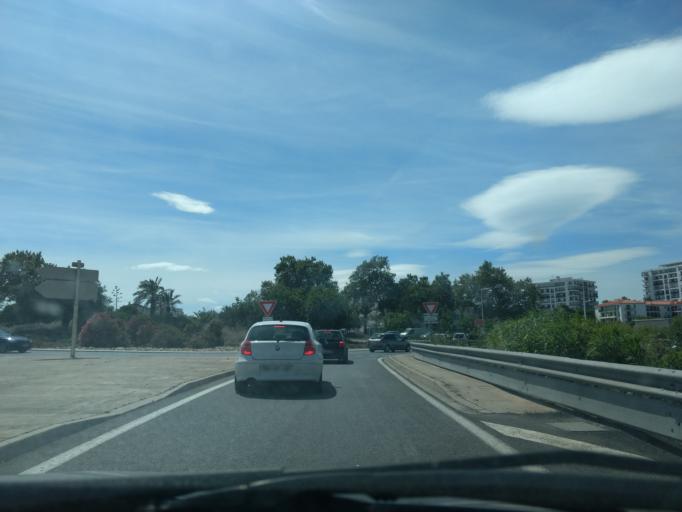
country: FR
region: Languedoc-Roussillon
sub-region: Departement des Pyrenees-Orientales
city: Perpignan
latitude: 42.6781
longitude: 2.9138
